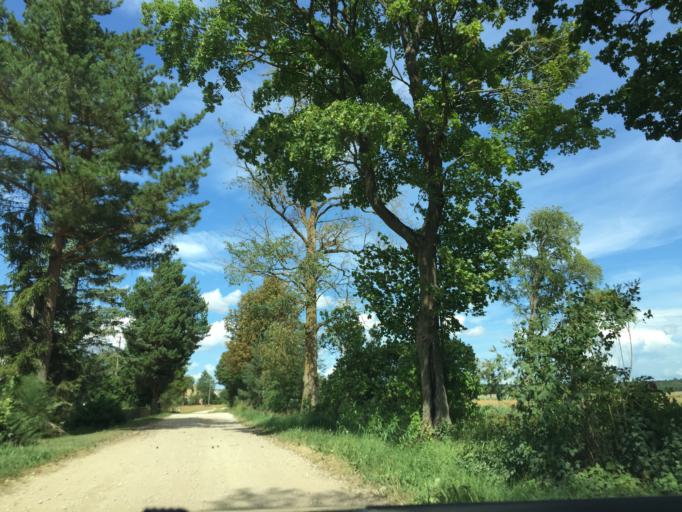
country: LT
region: Siauliu apskritis
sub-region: Joniskis
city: Joniskis
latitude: 56.3475
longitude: 23.6240
